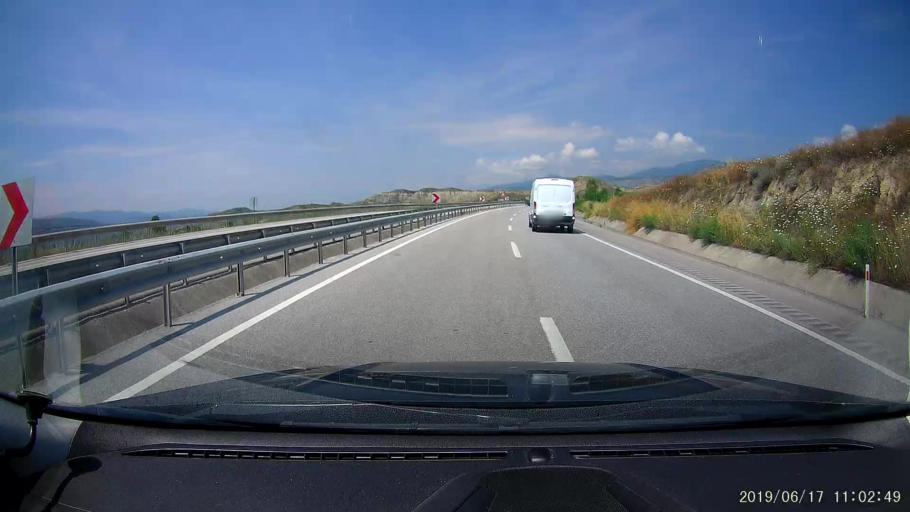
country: TR
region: Kastamonu
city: Tosya
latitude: 41.0150
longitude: 34.1277
